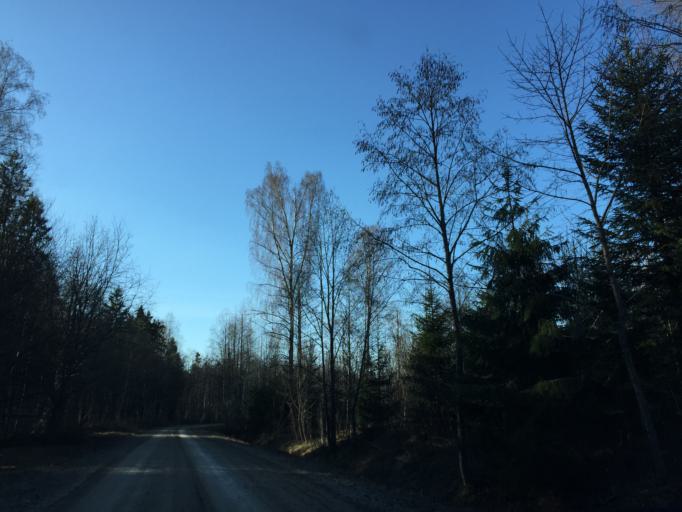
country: EE
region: Ida-Virumaa
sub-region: Sillamaee linn
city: Sillamae
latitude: 59.1484
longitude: 27.8049
